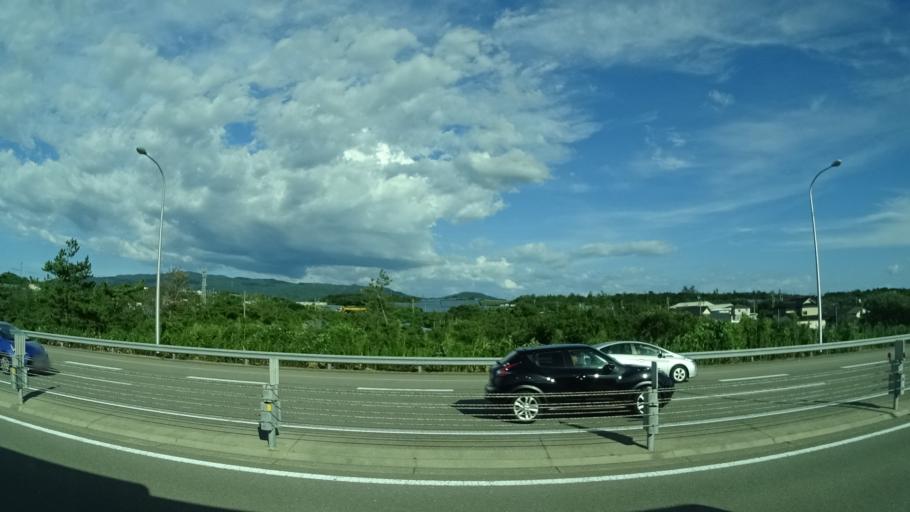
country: JP
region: Ishikawa
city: Tsubata
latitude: 36.7810
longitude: 136.7206
